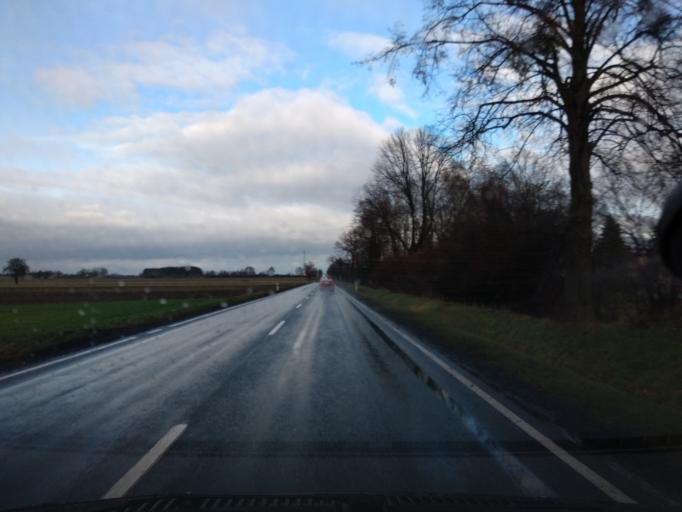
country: PL
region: Greater Poland Voivodeship
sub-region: Powiat koninski
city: Rychwal
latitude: 52.0449
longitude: 18.1623
